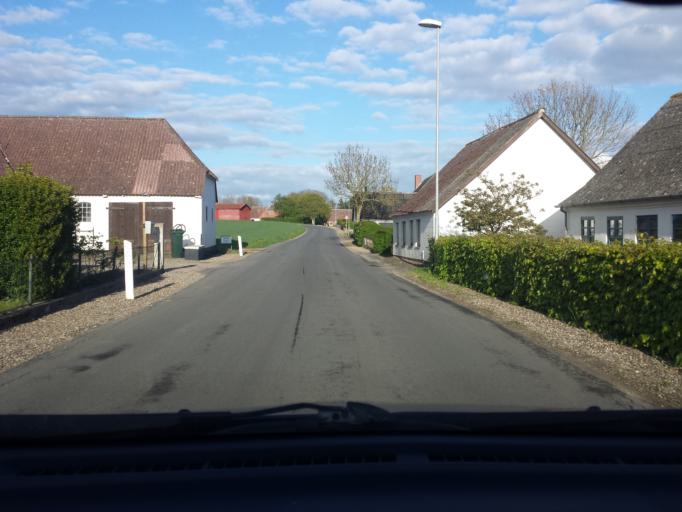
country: DK
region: South Denmark
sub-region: Langeland Kommune
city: Rudkobing
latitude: 54.9026
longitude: 10.7633
